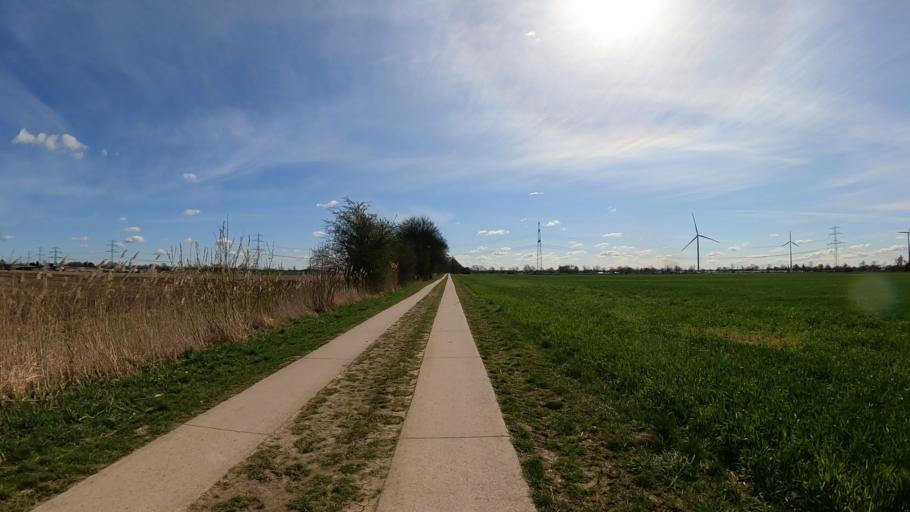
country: DE
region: Lower Saxony
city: Stelle
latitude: 53.4629
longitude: 10.1033
